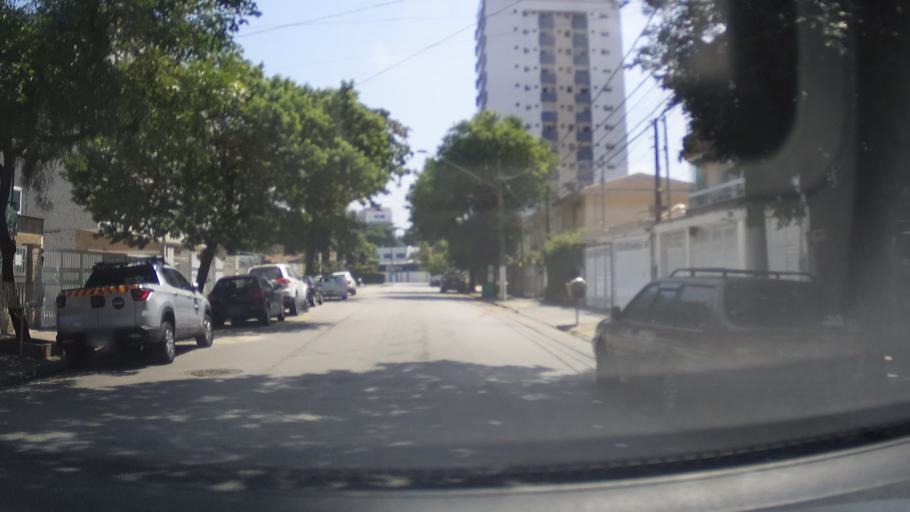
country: BR
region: Sao Paulo
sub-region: Santos
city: Santos
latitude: -23.9817
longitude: -46.2985
